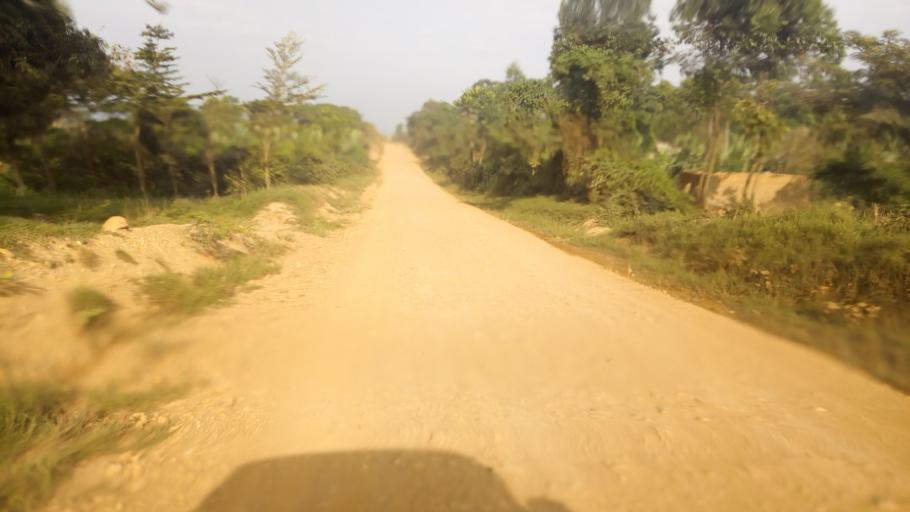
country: UG
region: Western Region
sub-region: Kanungu District
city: Ntungamo
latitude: -0.8347
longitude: 29.6764
